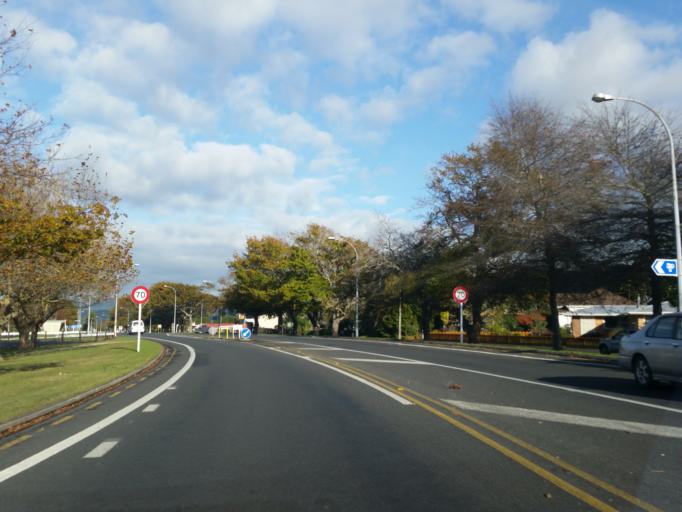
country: NZ
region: Waikato
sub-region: Hauraki District
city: Waihi
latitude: -37.3925
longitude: 175.8332
